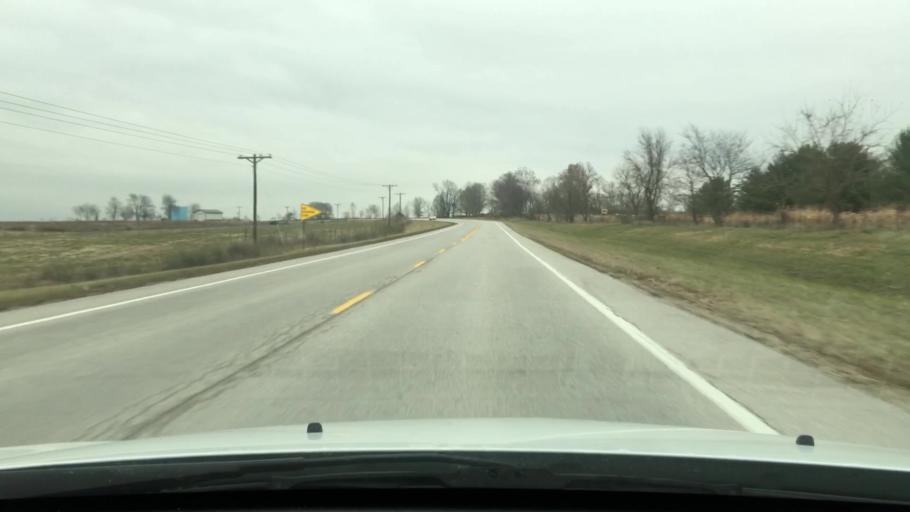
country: US
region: Illinois
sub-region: Pike County
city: Pittsfield
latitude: 39.5297
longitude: -90.9255
